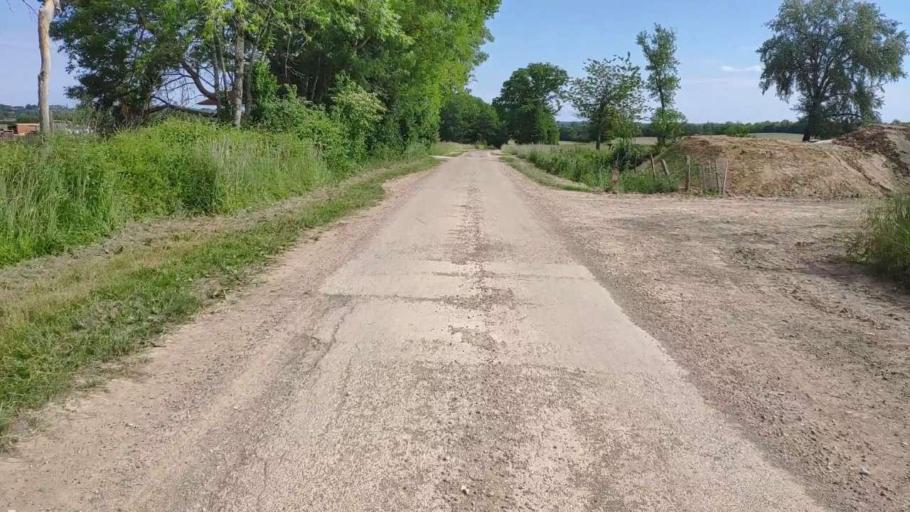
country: FR
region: Franche-Comte
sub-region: Departement du Jura
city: Bletterans
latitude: 46.7138
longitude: 5.4449
